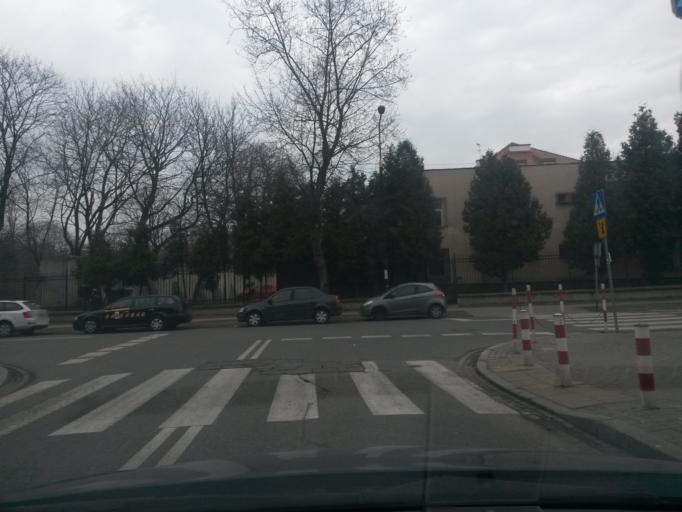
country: PL
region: Masovian Voivodeship
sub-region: Warszawa
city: Mokotow
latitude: 52.2095
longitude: 21.0387
